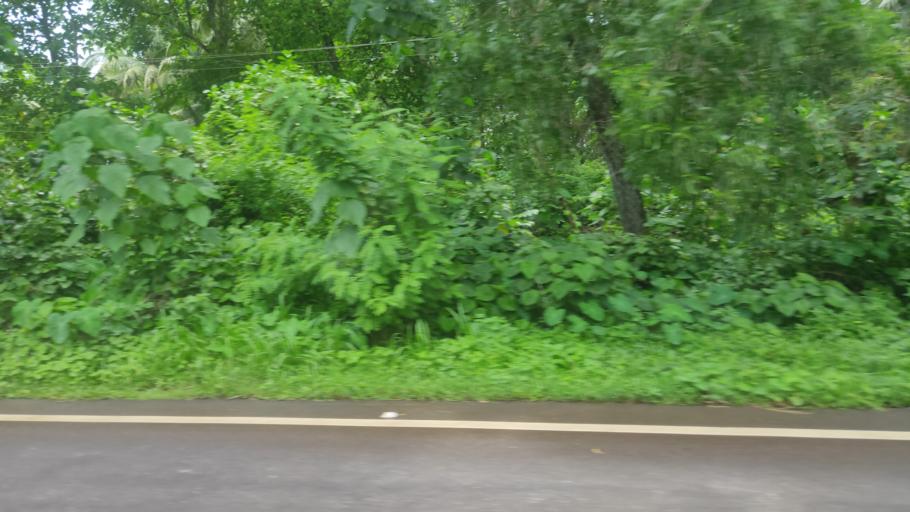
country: IN
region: Kerala
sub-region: Kasaragod District
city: Manjeshwara
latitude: 12.7394
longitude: 74.9341
